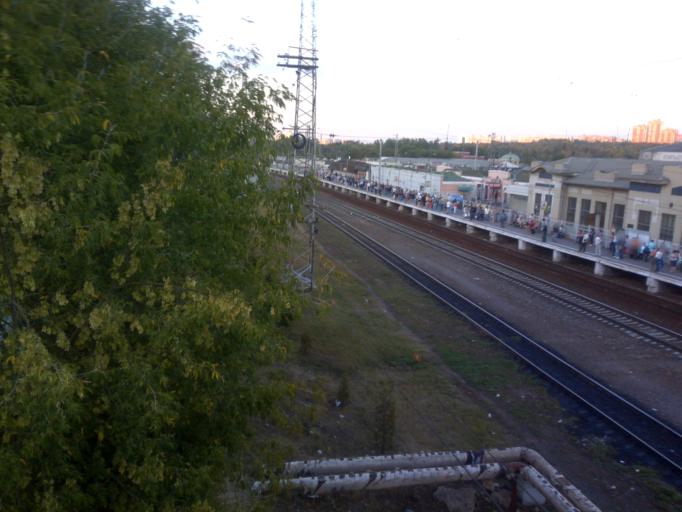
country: RU
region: Moscow
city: Orekhovo-Borisovo Severnoye
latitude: 55.6181
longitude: 37.6671
